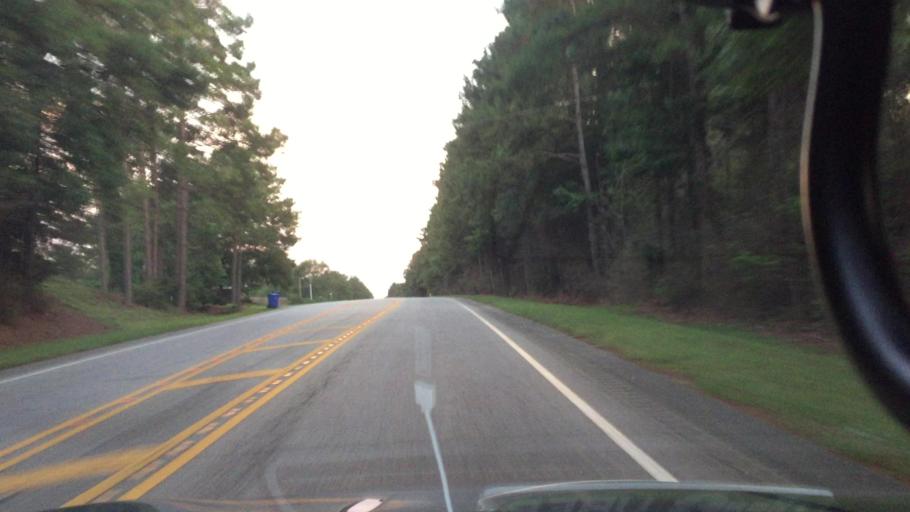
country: US
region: Alabama
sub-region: Coffee County
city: New Brockton
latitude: 31.3956
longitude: -85.8791
